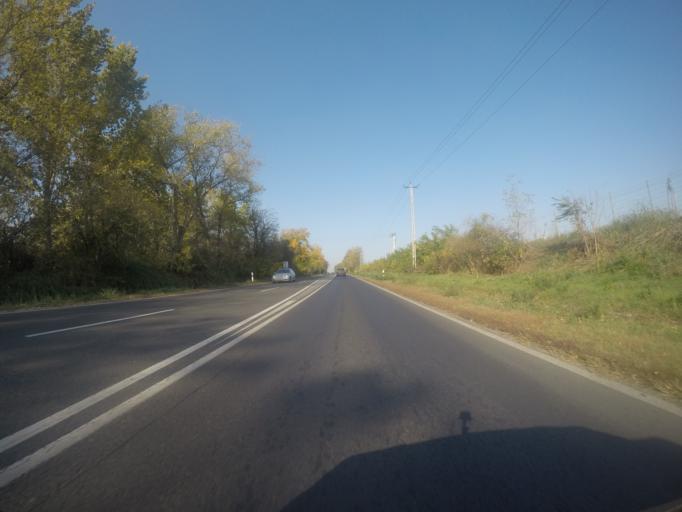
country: HU
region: Tolna
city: Dunafoldvar
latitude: 46.8356
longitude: 18.9095
